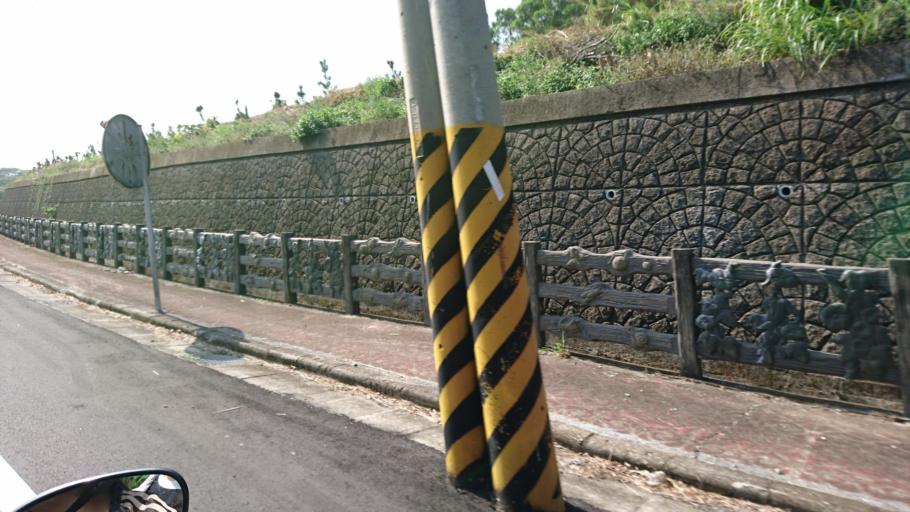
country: TW
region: Taiwan
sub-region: Hsinchu
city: Hsinchu
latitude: 24.7178
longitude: 120.9237
